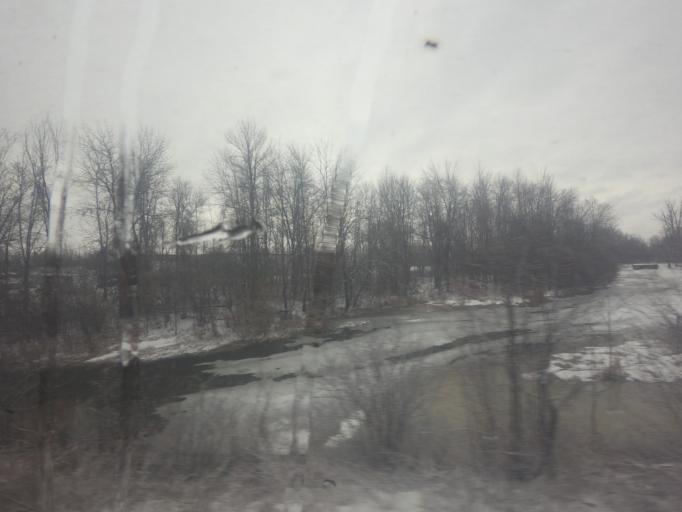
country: CA
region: Ontario
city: Bells Corners
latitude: 45.1909
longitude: -75.8207
